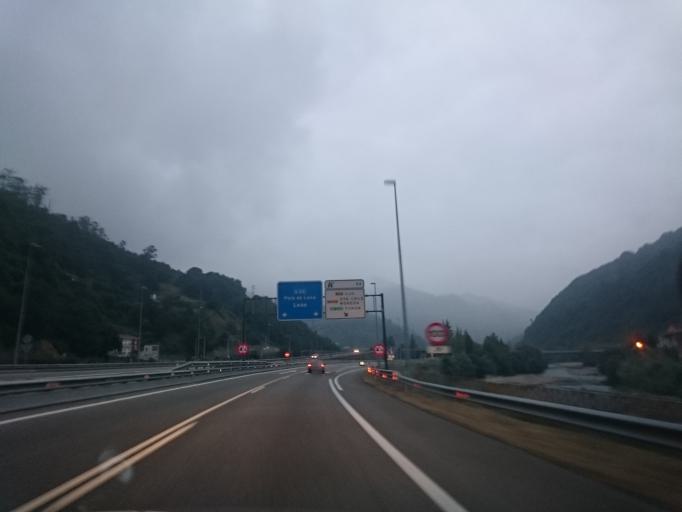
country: ES
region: Asturias
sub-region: Province of Asturias
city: Mieres
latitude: 43.2044
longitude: -5.7873
